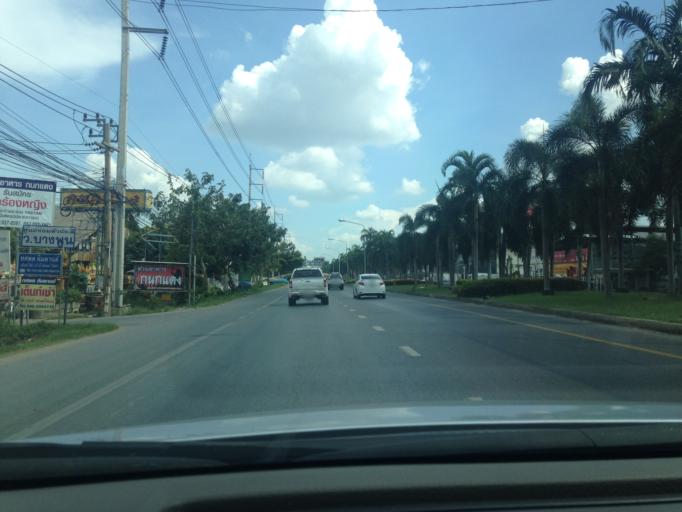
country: TH
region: Phra Nakhon Si Ayutthaya
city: Ban Bang Kadi Pathum Thani
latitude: 13.9883
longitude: 100.5851
